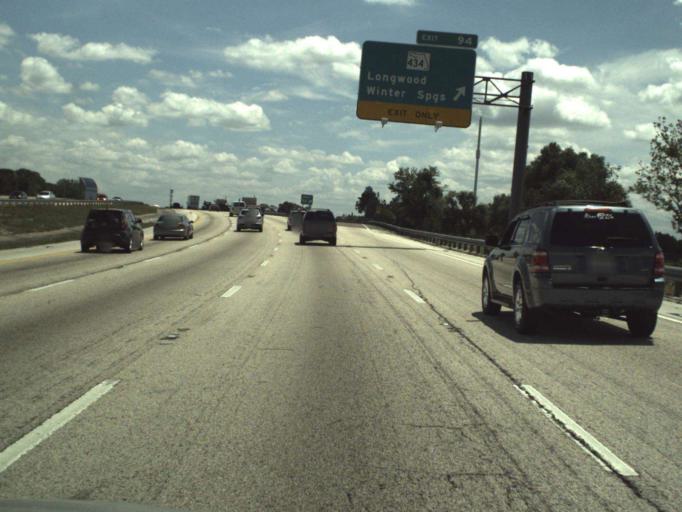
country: US
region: Florida
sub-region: Seminole County
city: Wekiwa Springs
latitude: 28.6937
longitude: -81.3887
